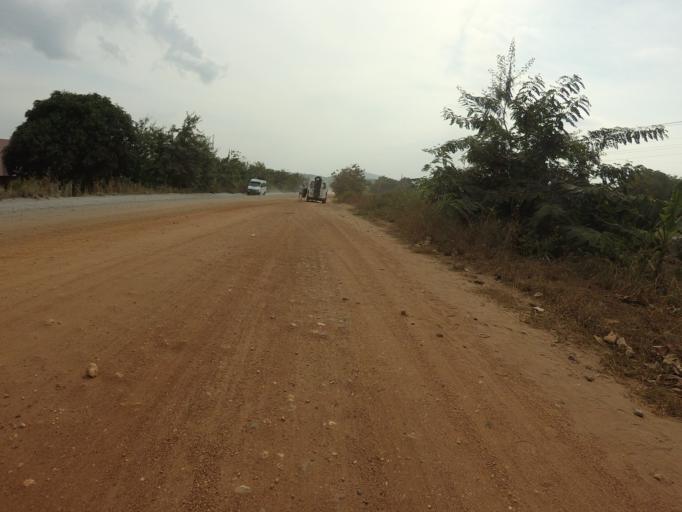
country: GH
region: Volta
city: Ho
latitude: 6.6799
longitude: 0.3231
